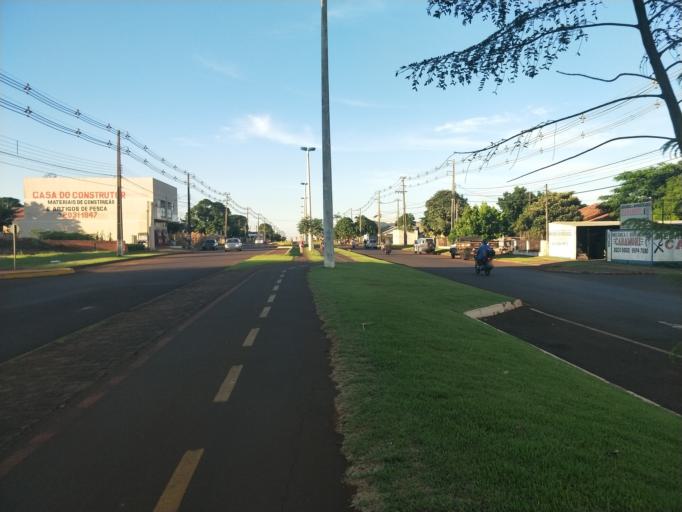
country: BR
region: Parana
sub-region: Marechal Candido Rondon
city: Marechal Candido Rondon
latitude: -24.5509
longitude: -54.0459
